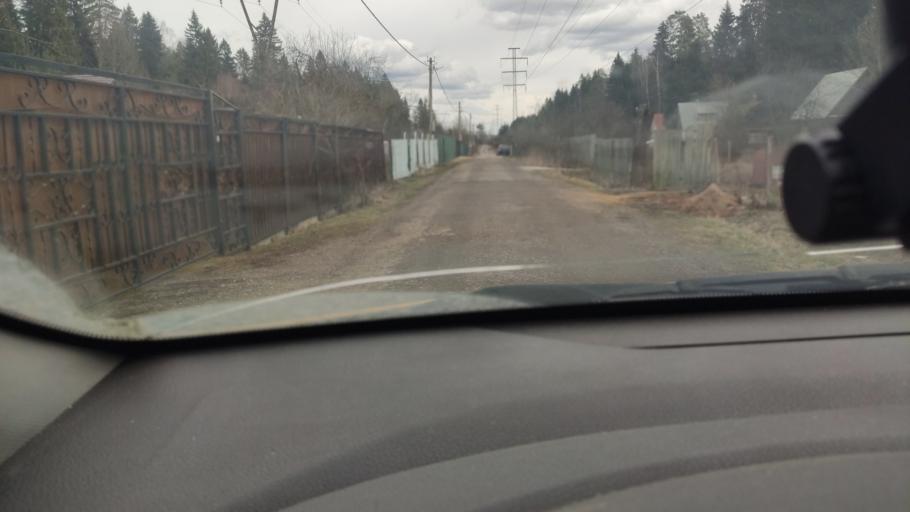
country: RU
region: Moskovskaya
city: Chupryakovo
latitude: 55.5827
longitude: 36.6094
